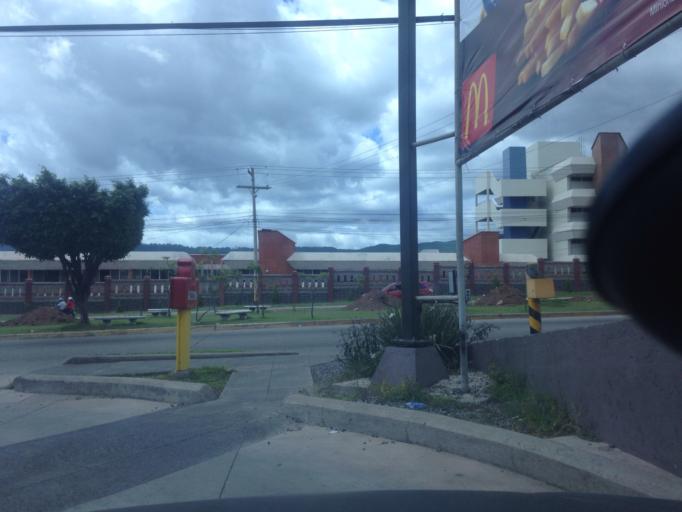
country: HN
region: Francisco Morazan
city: Tegucigalpa
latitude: 14.0832
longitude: -87.1674
